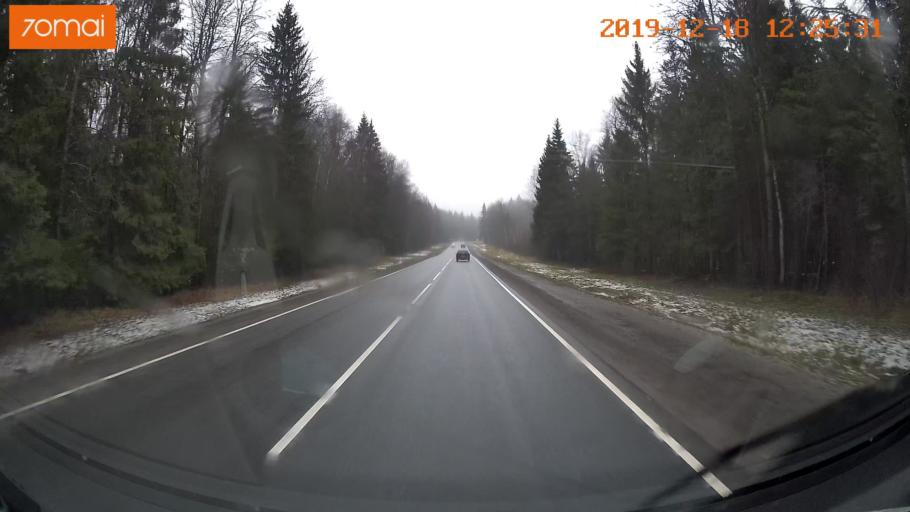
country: RU
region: Moskovskaya
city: Novopetrovskoye
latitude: 56.0391
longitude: 36.4993
